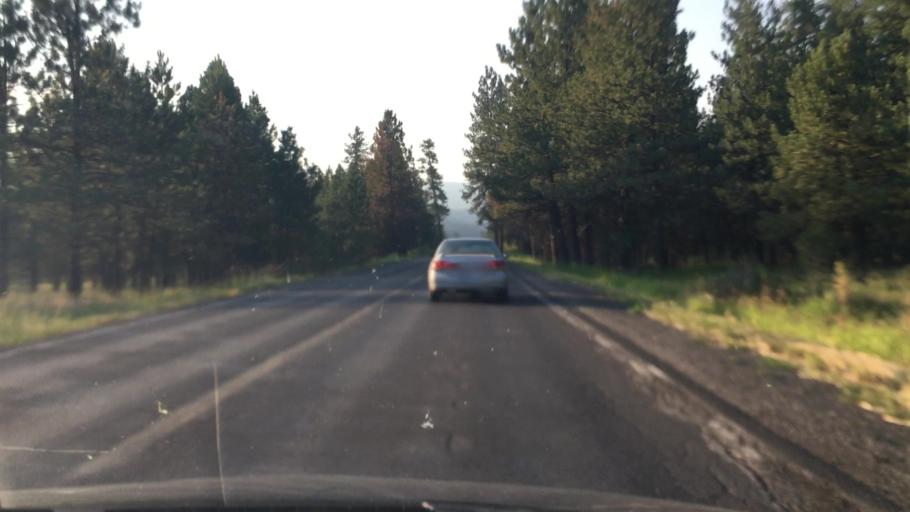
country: US
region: Idaho
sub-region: Valley County
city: McCall
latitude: 44.9392
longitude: -116.1663
